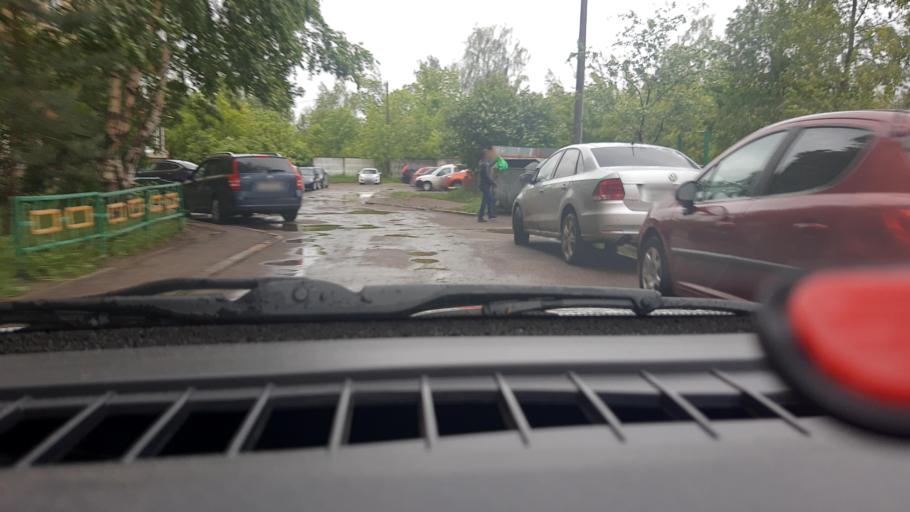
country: RU
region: Nizjnij Novgorod
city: Gorbatovka
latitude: 56.2400
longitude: 43.8240
